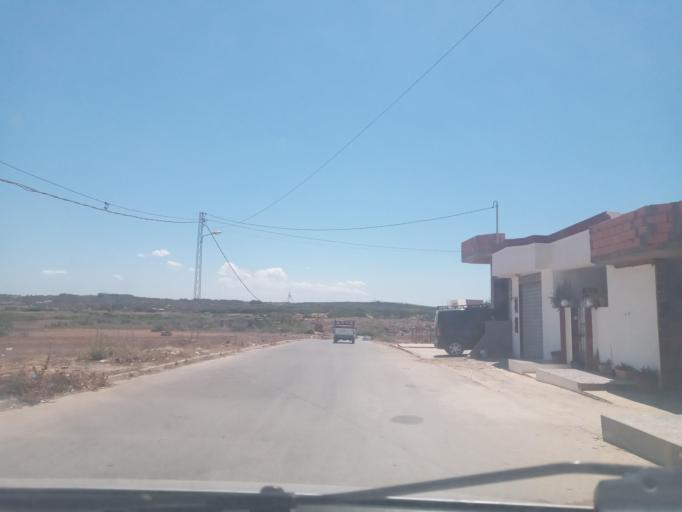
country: TN
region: Nabul
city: El Haouaria
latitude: 37.0539
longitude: 10.9911
